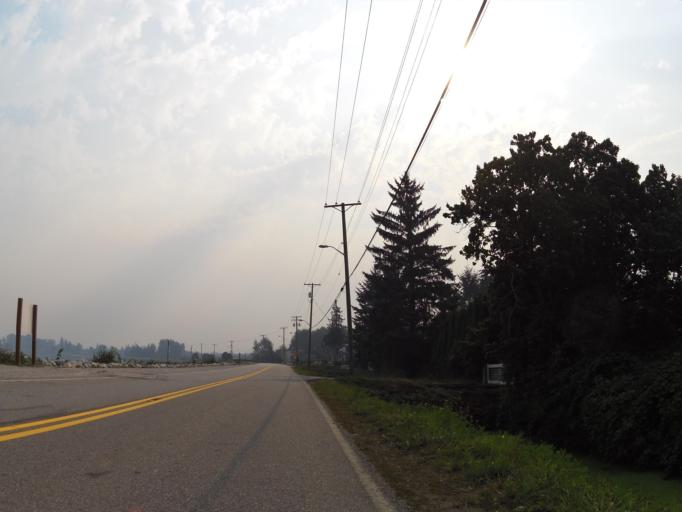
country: CA
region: British Columbia
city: New Westminster
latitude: 49.1794
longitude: -122.9808
